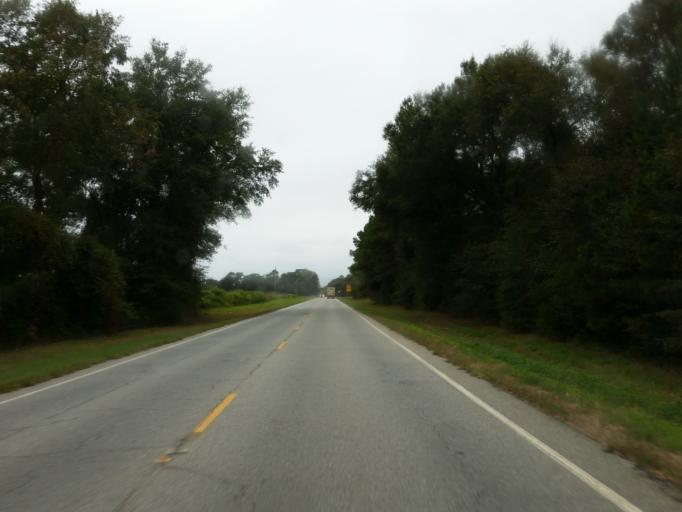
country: US
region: Georgia
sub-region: Cook County
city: Adel
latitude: 31.1255
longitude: -83.3318
